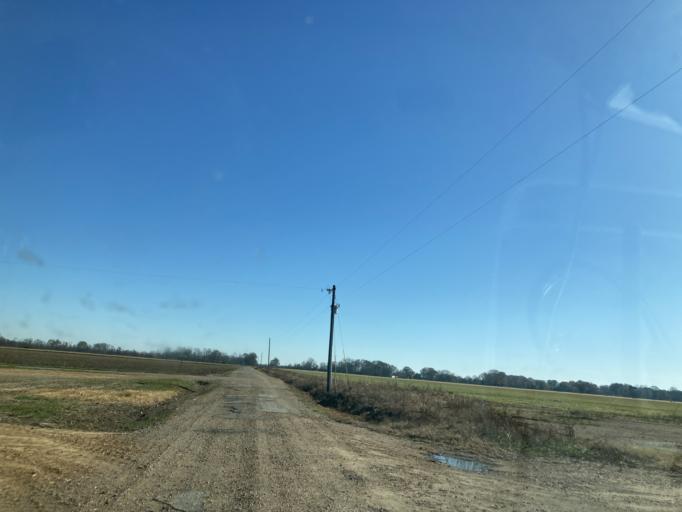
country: US
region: Mississippi
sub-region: Sharkey County
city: Rolling Fork
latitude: 32.8573
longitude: -90.7108
